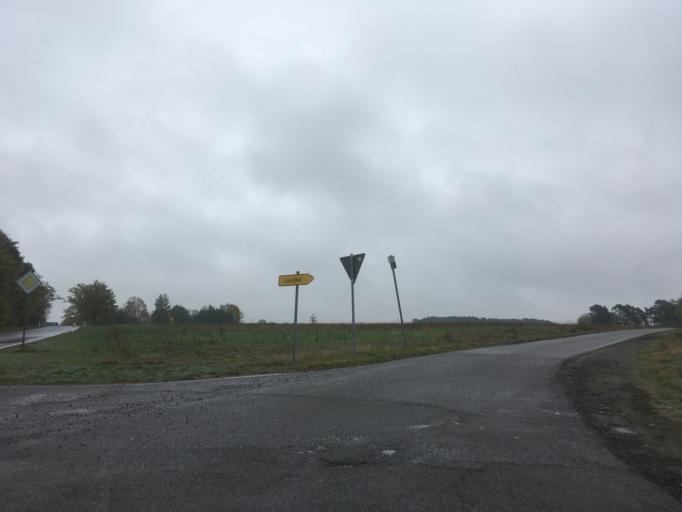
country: DE
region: Brandenburg
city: Neu Zauche
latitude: 52.0358
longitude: 14.0586
